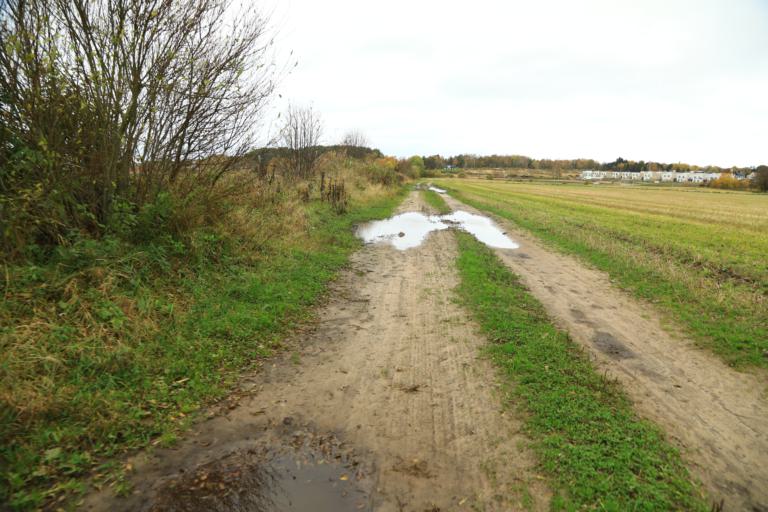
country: SE
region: Halland
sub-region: Varbergs Kommun
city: Traslovslage
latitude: 57.0968
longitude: 12.3018
